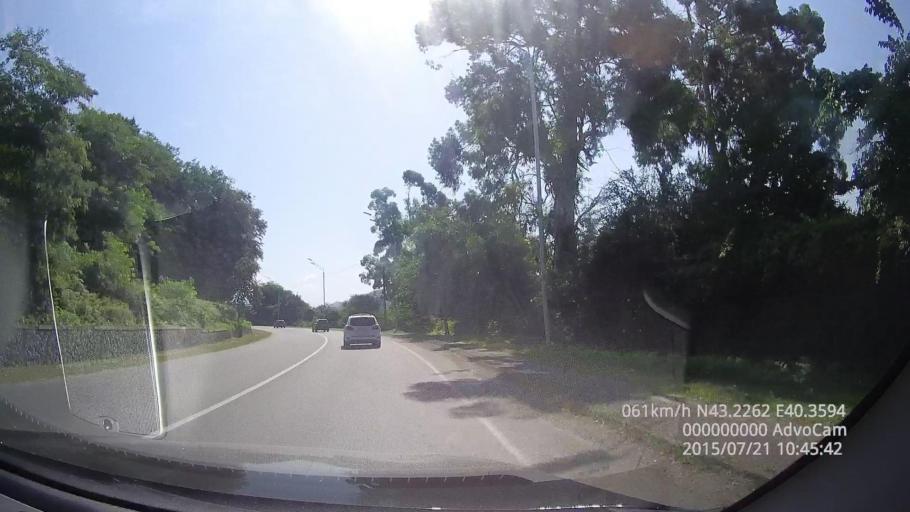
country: GE
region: Abkhazia
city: Bich'vinta
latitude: 43.2262
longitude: 40.3598
